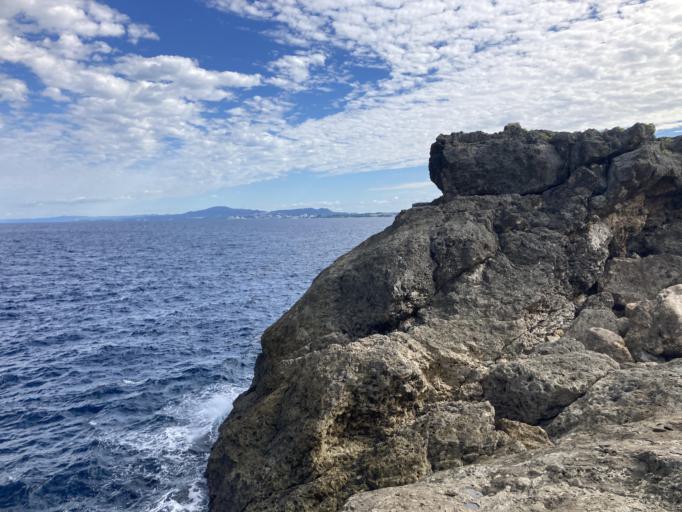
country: JP
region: Okinawa
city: Ishikawa
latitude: 26.4408
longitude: 127.7144
